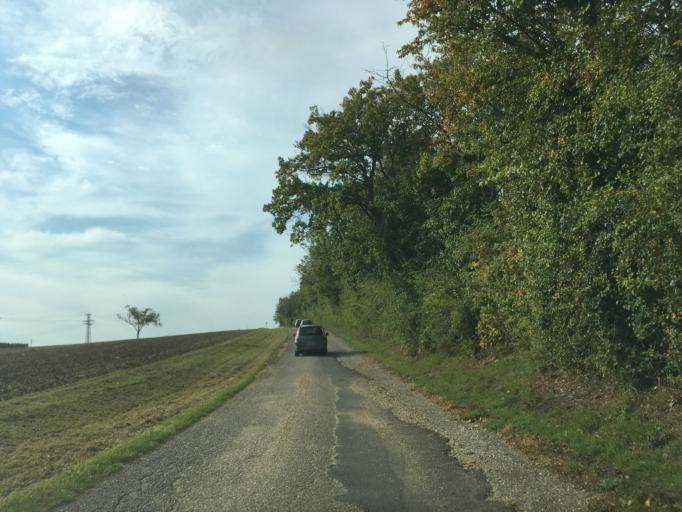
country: AT
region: Burgenland
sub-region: Politischer Bezirk Neusiedl am See
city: Jois
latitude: 47.9713
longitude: 16.8135
